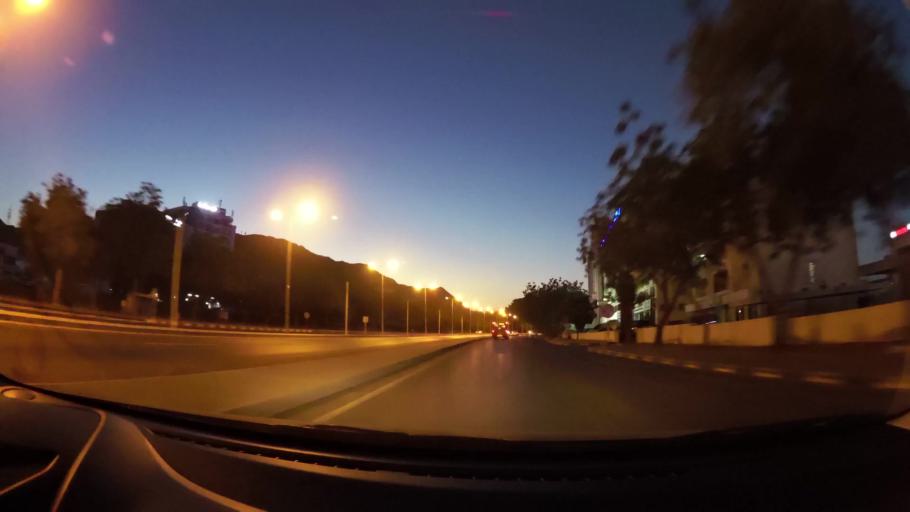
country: OM
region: Muhafazat Masqat
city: Muscat
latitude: 23.5986
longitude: 58.5385
